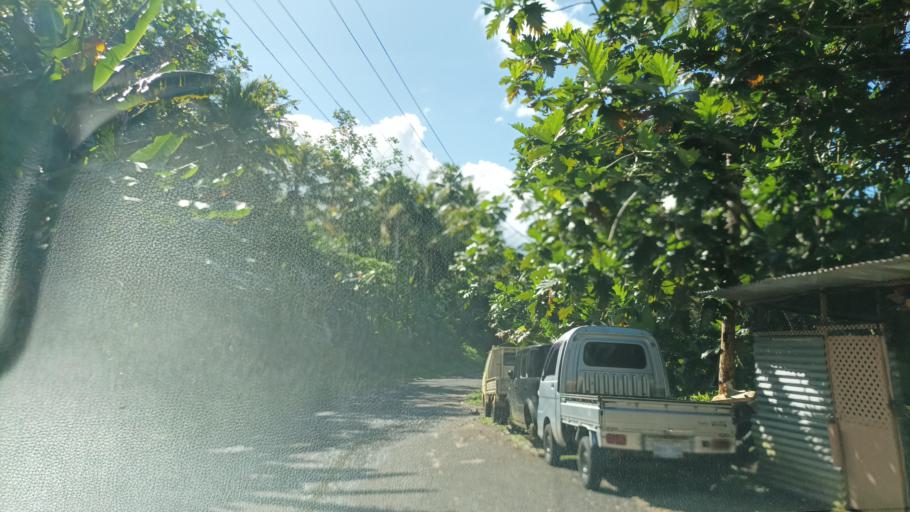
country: FM
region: Pohnpei
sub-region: Madolenihm Municipality
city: Madolenihm Municipality Government
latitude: 6.8536
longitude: 158.2966
